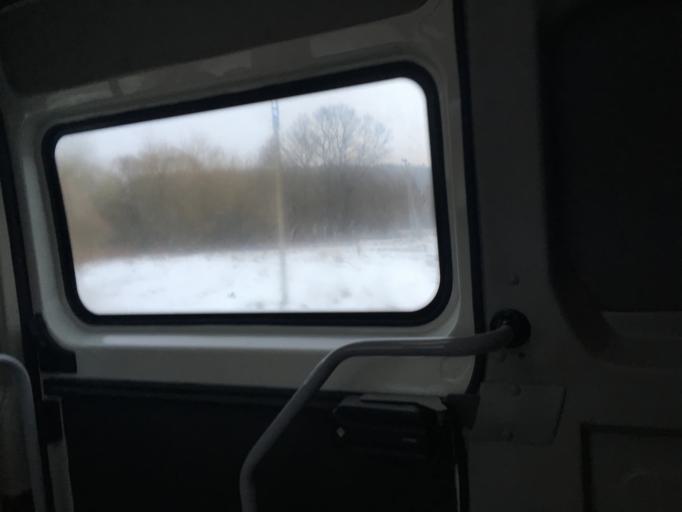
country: RU
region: Tula
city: Krapivna
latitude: 54.1123
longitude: 37.2135
